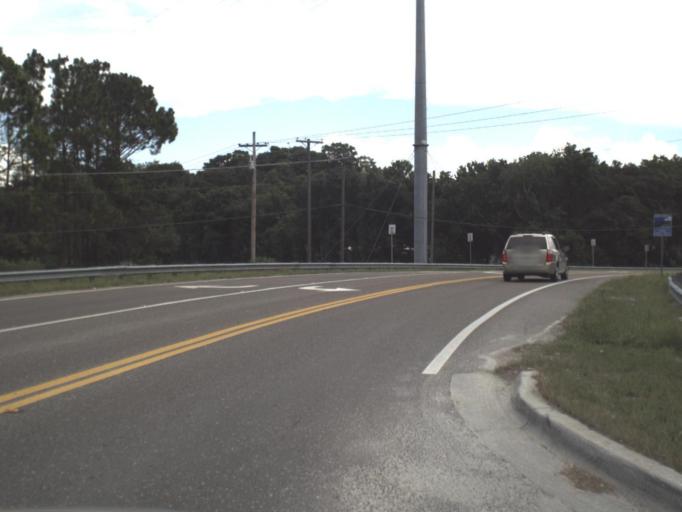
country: US
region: Florida
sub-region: Pasco County
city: Trinity
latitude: 28.2166
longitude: -82.6834
